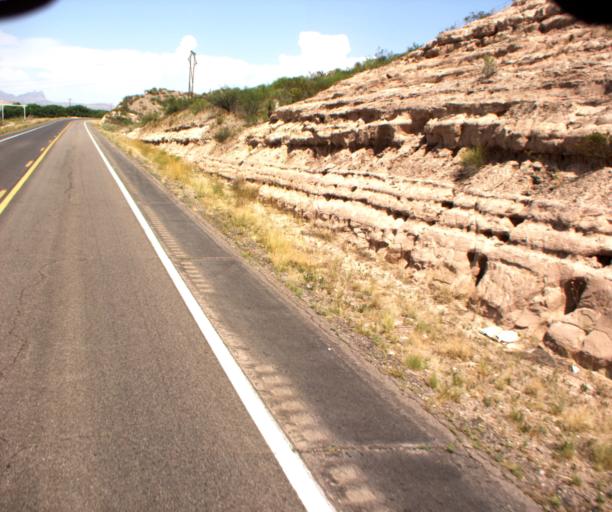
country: US
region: Arizona
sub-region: Greenlee County
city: Clifton
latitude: 32.7411
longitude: -109.1356
